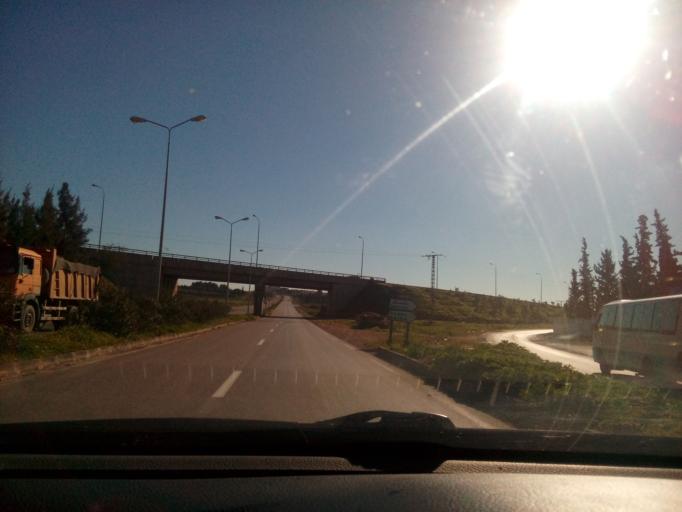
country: DZ
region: Relizane
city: Relizane
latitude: 35.7175
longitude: 0.5076
